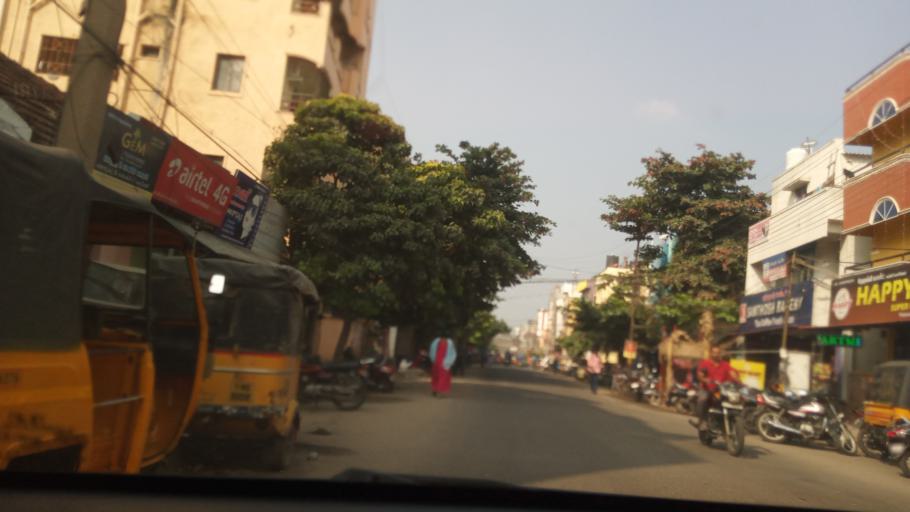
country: IN
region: Tamil Nadu
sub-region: Coimbatore
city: Coimbatore
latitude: 10.9998
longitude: 76.9536
